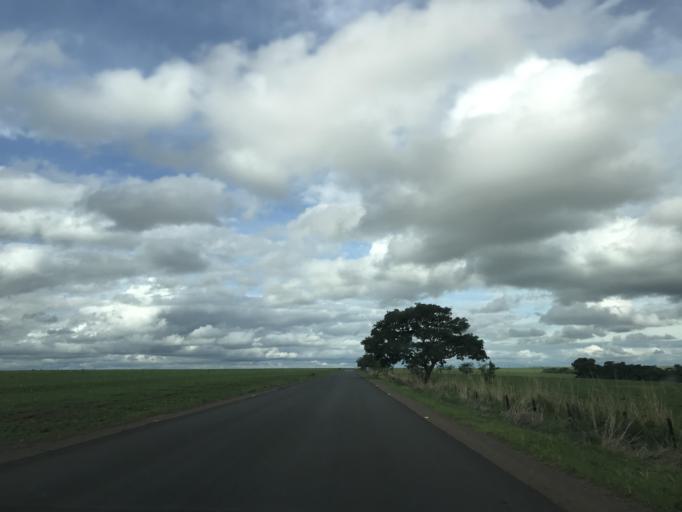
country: BR
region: Goias
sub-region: Vianopolis
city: Vianopolis
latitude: -16.9641
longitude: -48.6444
